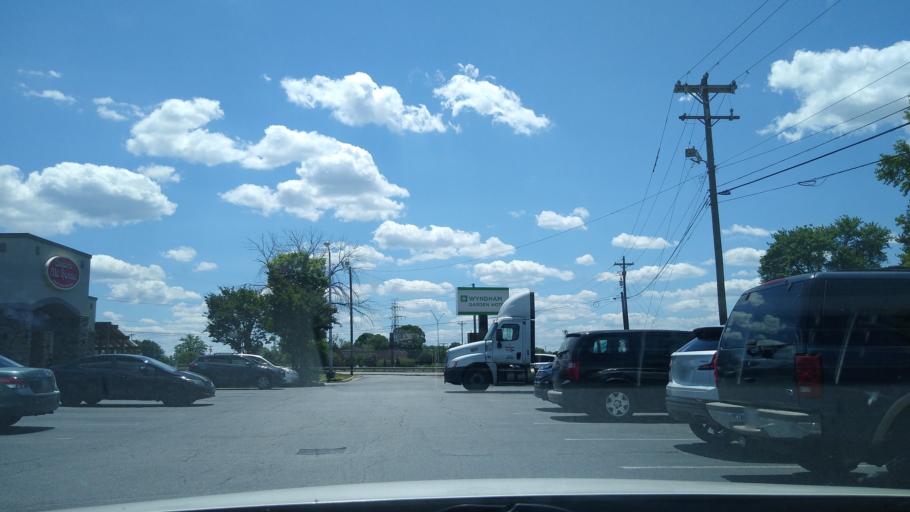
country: US
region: North Carolina
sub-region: Guilford County
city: Jamestown
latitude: 36.0646
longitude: -79.9095
